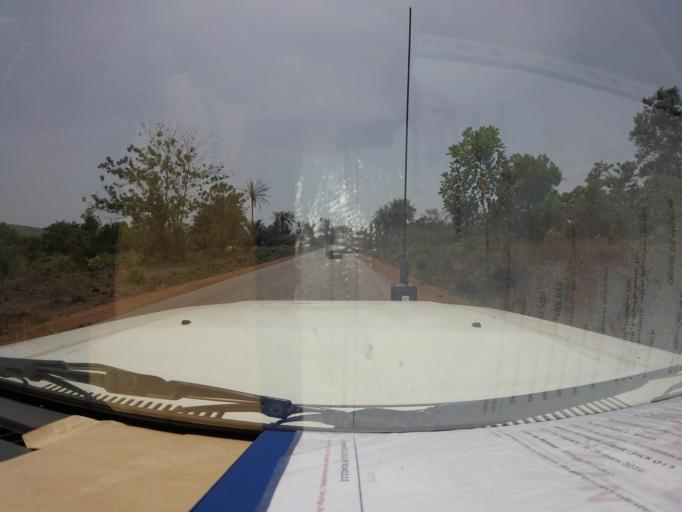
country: GN
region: Kindia
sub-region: Coyah
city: Coyah
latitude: 9.8015
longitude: -13.2867
